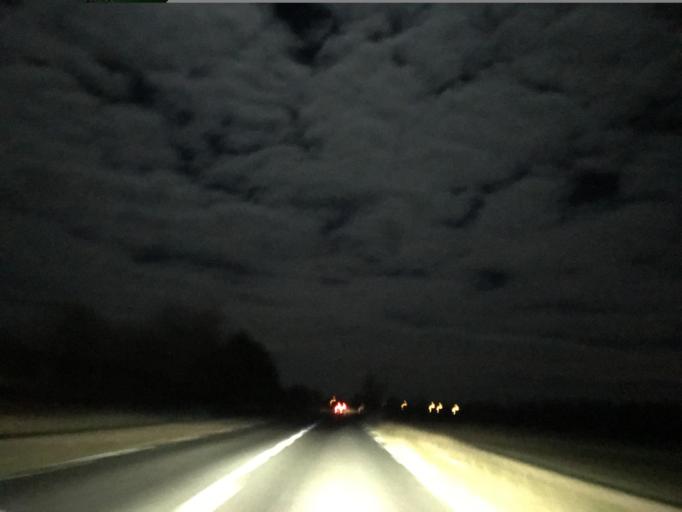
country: FR
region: Auvergne
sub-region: Departement de l'Allier
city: Hauterive
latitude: 46.0872
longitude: 3.4425
